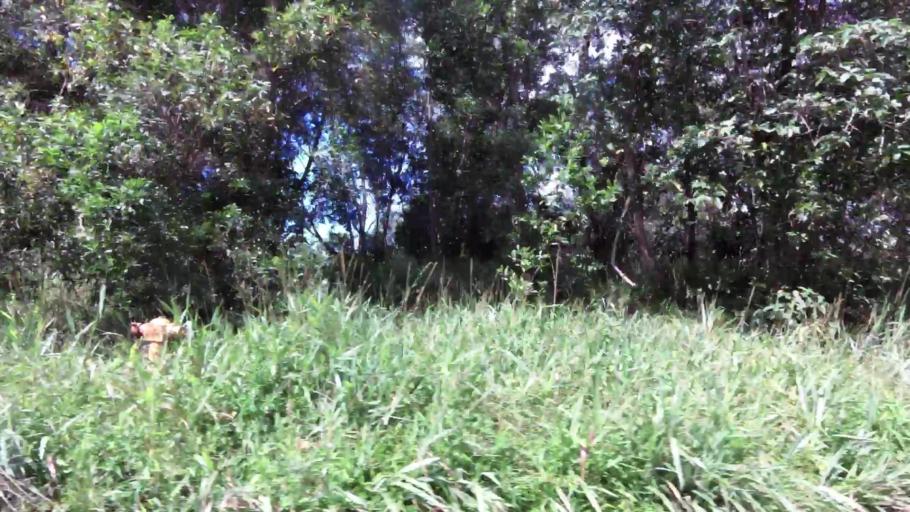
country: BN
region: Brunei and Muara
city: Bandar Seri Begawan
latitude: 4.9687
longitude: 114.9406
